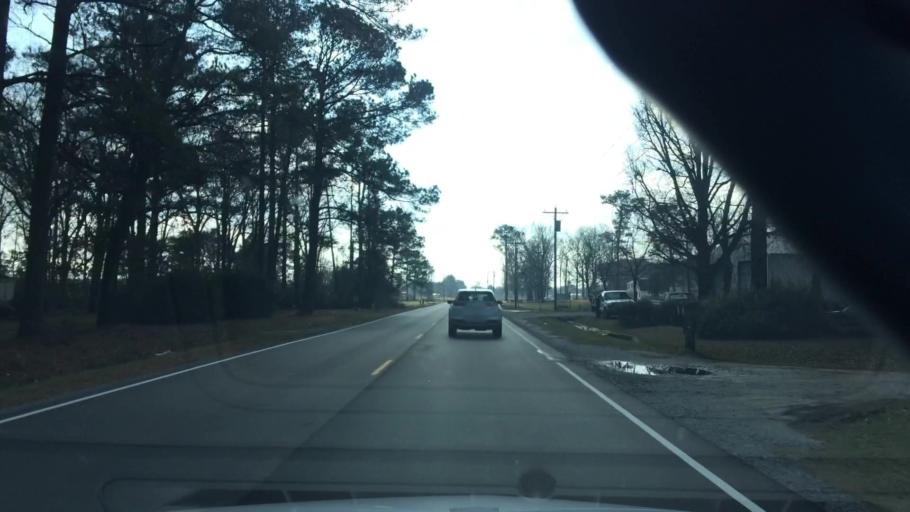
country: US
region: North Carolina
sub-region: Duplin County
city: Beulaville
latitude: 34.9621
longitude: -77.7643
